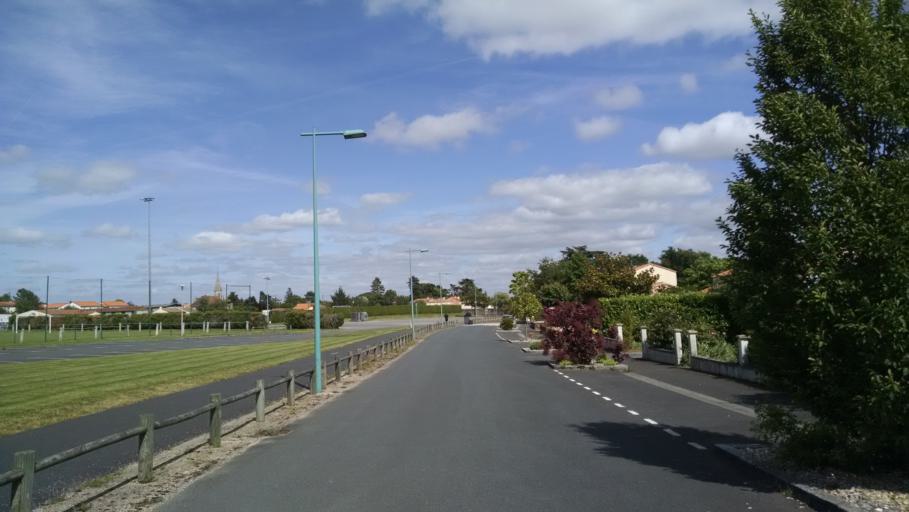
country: FR
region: Pays de la Loire
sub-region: Departement de la Loire-Atlantique
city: Aigrefeuille-sur-Maine
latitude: 47.0755
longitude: -1.4073
